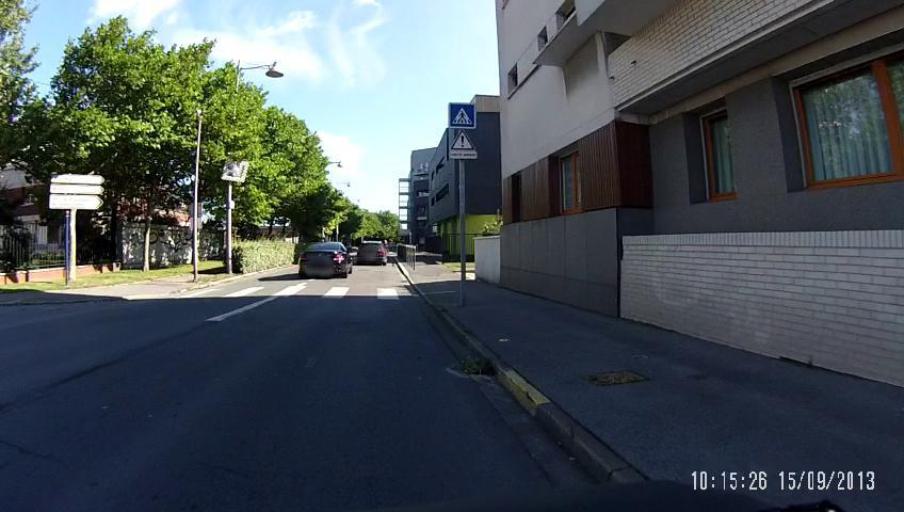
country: FR
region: Nord-Pas-de-Calais
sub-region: Departement du Nord
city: Dunkerque
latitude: 51.0425
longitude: 2.3766
